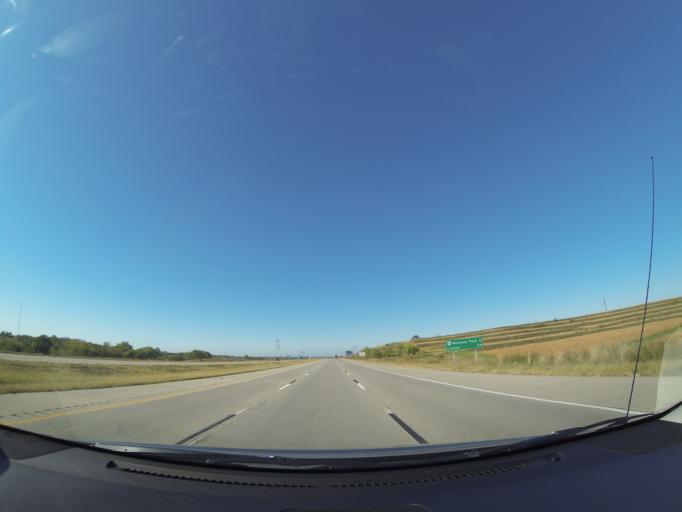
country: US
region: Nebraska
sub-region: Sarpy County
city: Gretna
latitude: 41.0898
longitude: -96.2635
